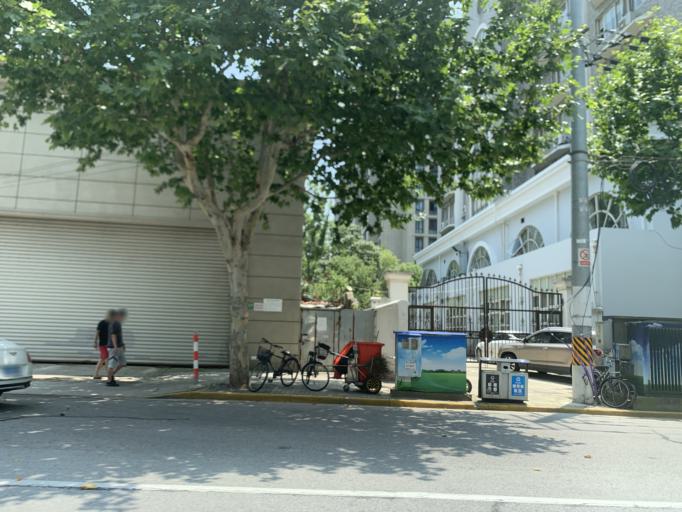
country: CN
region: Shanghai Shi
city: Pudong
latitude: 31.2156
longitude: 121.5107
